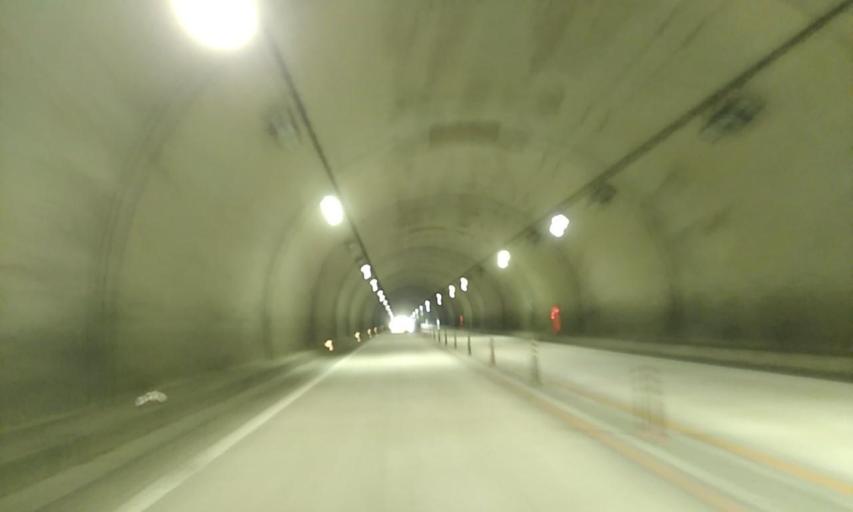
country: JP
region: Wakayama
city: Shingu
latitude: 33.5963
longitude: 135.9156
